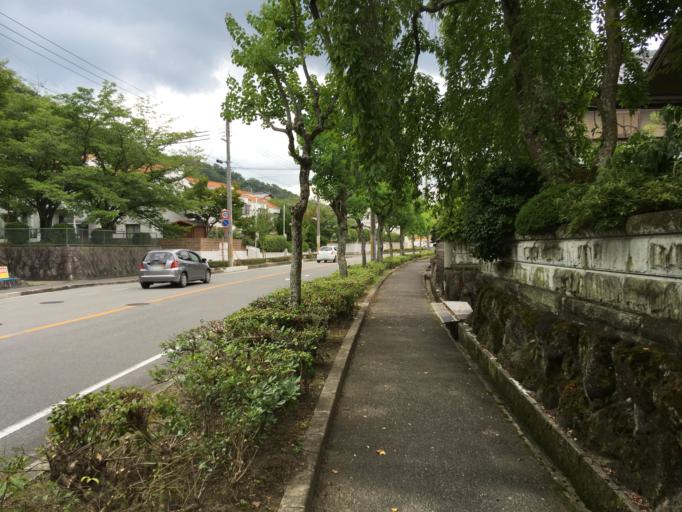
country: JP
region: Nara
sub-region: Ikoma-shi
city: Ikoma
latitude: 34.6789
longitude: 135.7186
